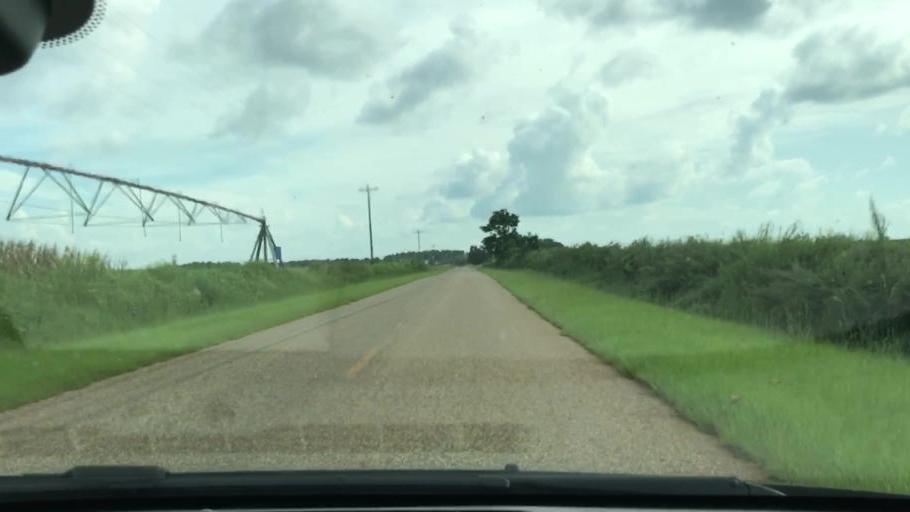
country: US
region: Georgia
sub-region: Clay County
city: Fort Gaines
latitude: 31.5279
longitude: -84.9545
